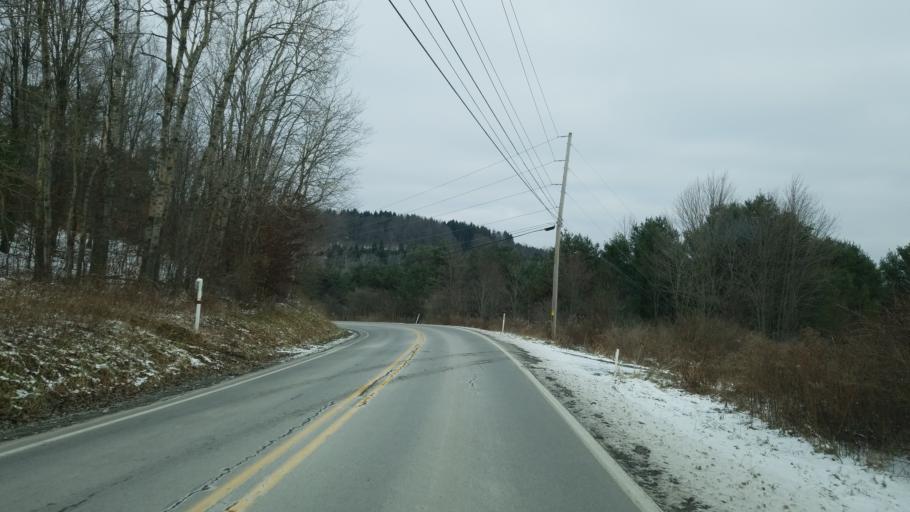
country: US
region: Pennsylvania
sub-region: Clearfield County
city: Sandy
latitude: 41.0751
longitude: -78.7354
